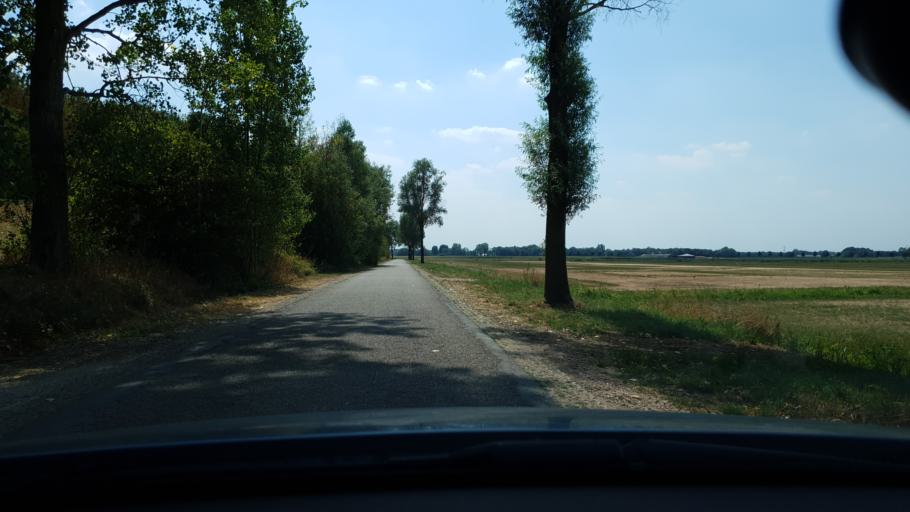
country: NL
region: Gelderland
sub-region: Gemeente Wijchen
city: Bergharen
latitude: 51.8519
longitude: 5.6874
